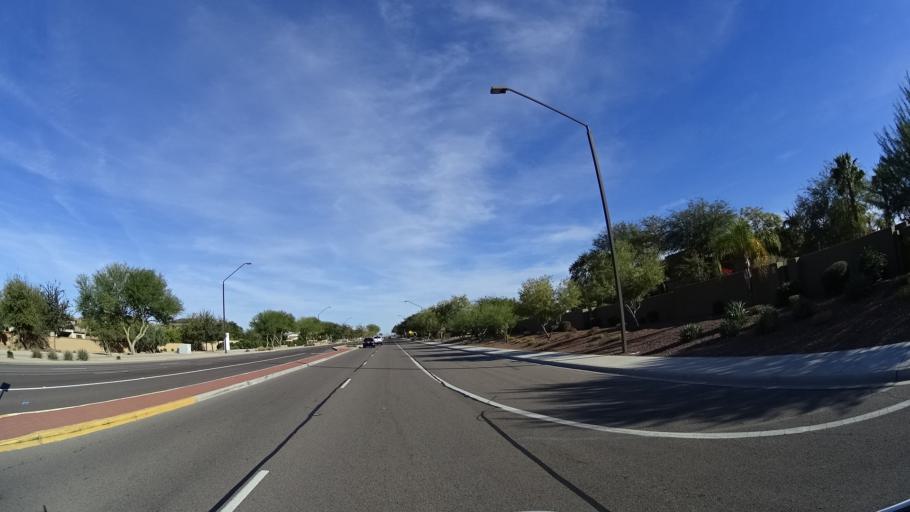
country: US
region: Arizona
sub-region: Maricopa County
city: Queen Creek
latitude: 33.2192
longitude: -111.7088
